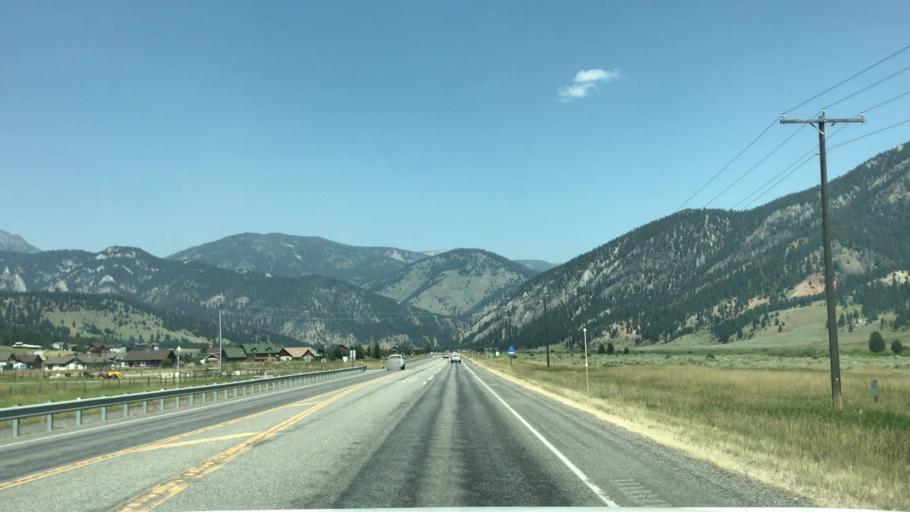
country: US
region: Montana
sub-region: Gallatin County
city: Big Sky
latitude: 45.2356
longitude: -111.2508
